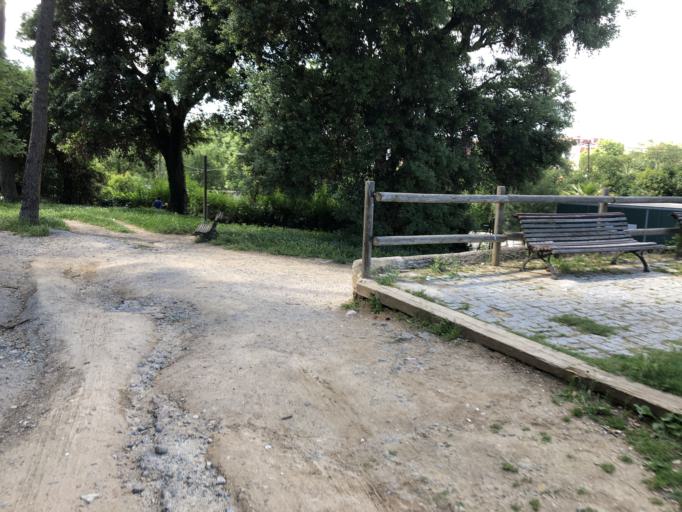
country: ES
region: Catalonia
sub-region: Provincia de Barcelona
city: Rubi
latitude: 41.4931
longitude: 2.0411
